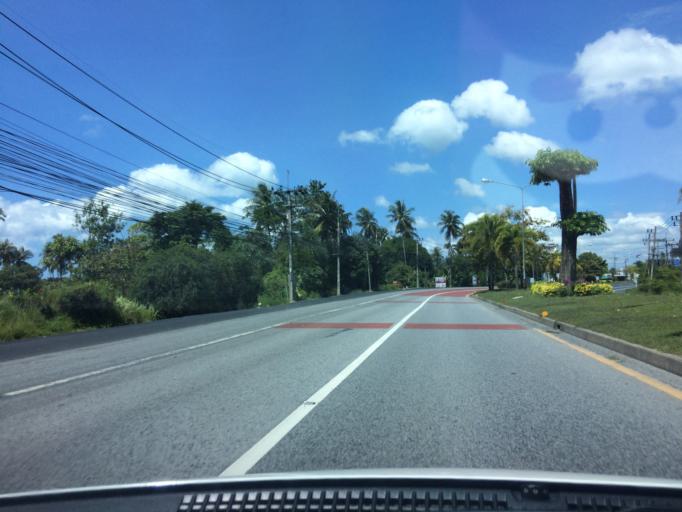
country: TH
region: Phuket
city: Thalang
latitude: 8.1723
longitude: 98.2986
